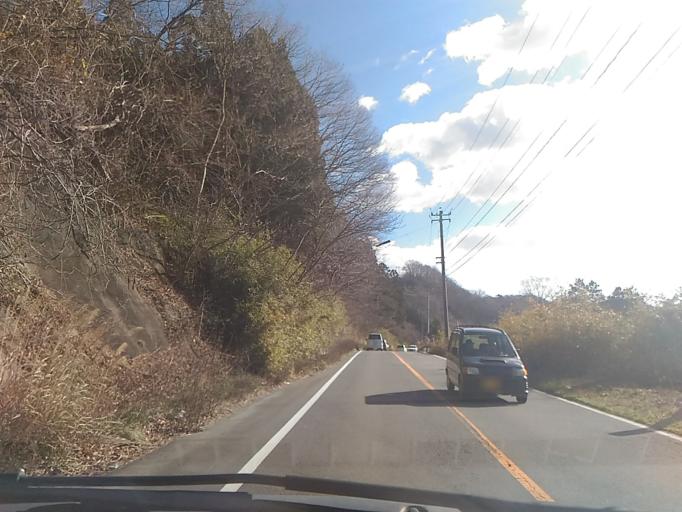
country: JP
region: Fukushima
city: Iwaki
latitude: 37.0083
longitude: 140.7809
